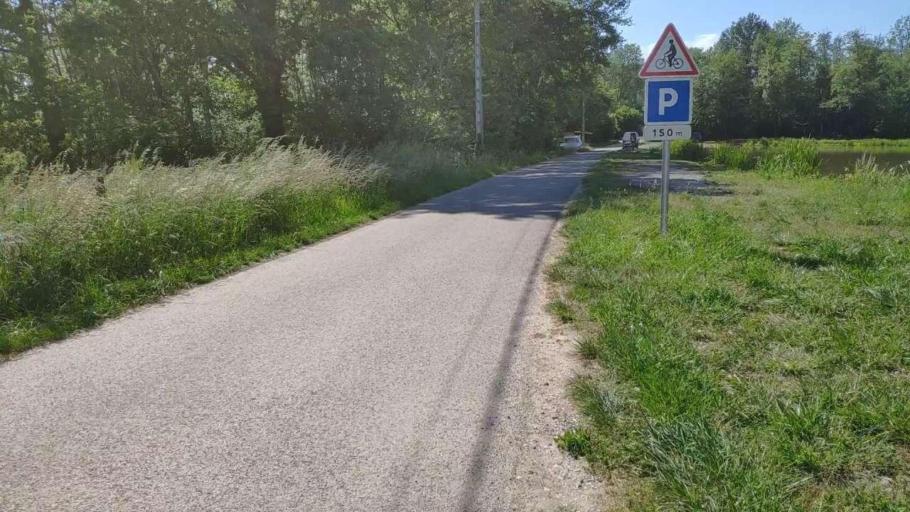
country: FR
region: Franche-Comte
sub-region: Departement du Jura
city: Bletterans
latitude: 46.7658
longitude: 5.4612
